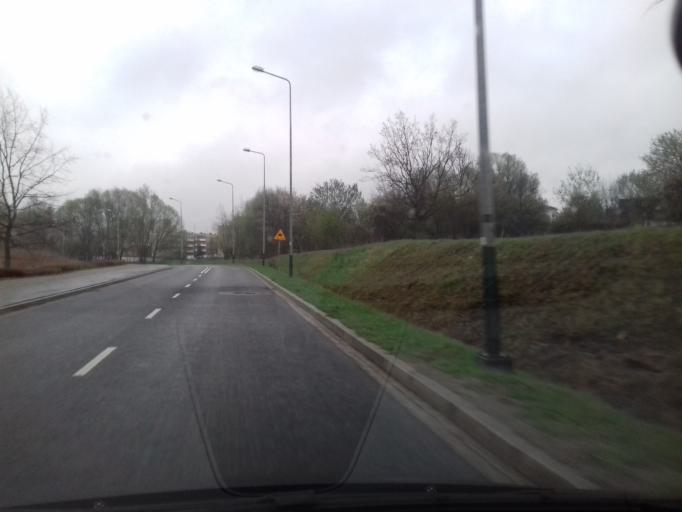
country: PL
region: Lesser Poland Voivodeship
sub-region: Krakow
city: Krakow
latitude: 50.0245
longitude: 19.9539
